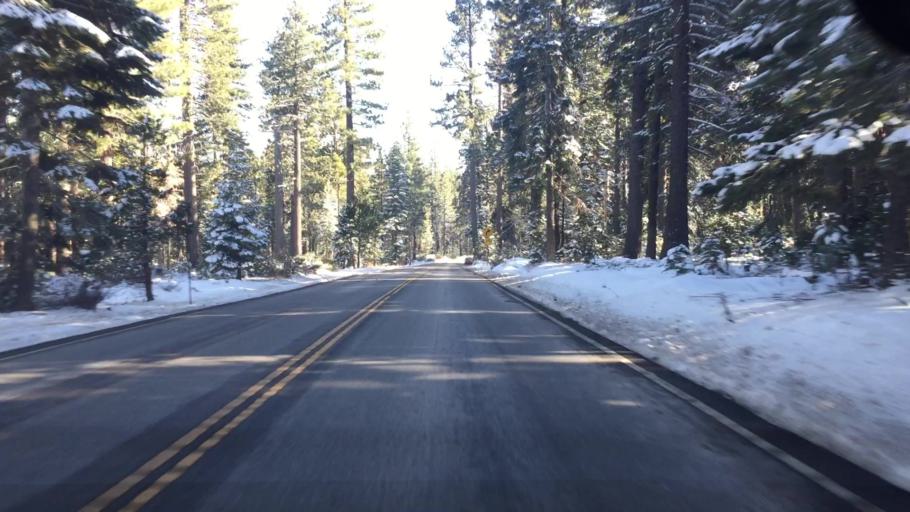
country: US
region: California
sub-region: Placer County
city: Tahoma
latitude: 39.0553
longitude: -120.1185
